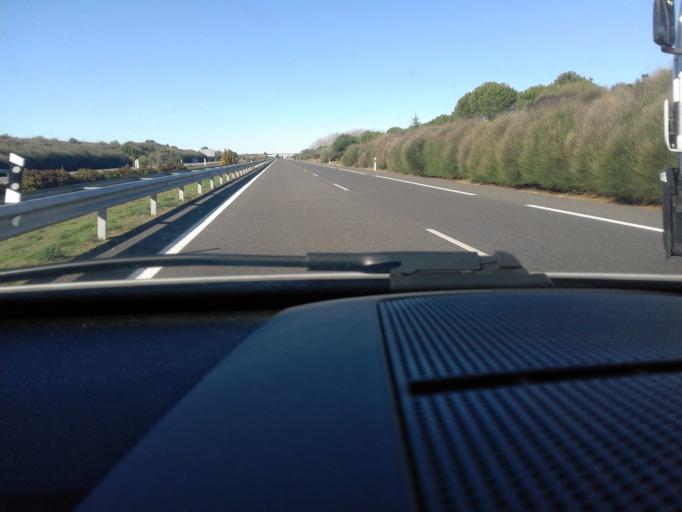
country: ES
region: Castille and Leon
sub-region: Provincia de Leon
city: Bercianos del Real Camino
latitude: 42.3973
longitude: -5.1582
